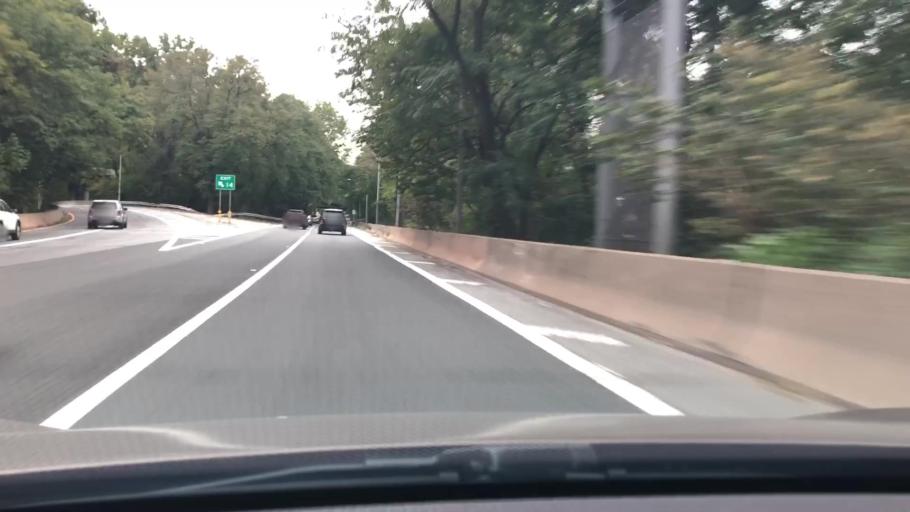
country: US
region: New Jersey
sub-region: Bergen County
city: Fort Lee
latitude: 40.8478
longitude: -73.9453
